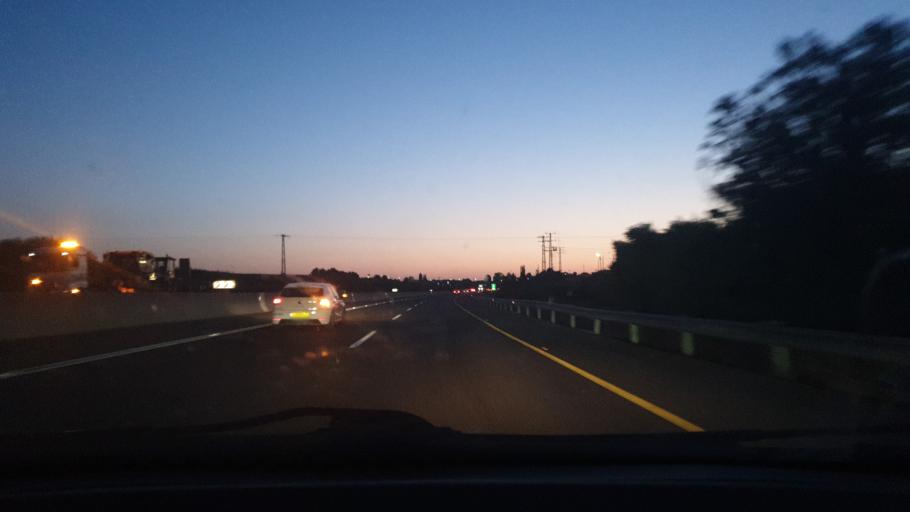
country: IL
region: Central District
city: Gedera
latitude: 31.7970
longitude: 34.7900
